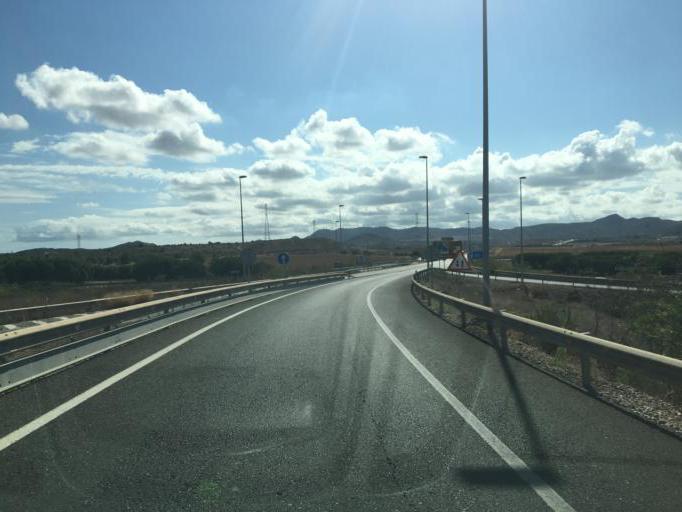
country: ES
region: Murcia
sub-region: Murcia
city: Cartagena
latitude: 37.6269
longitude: -0.9454
